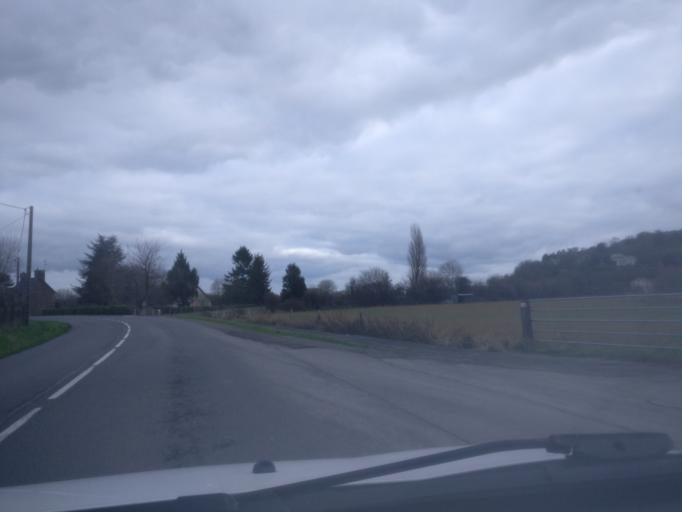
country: FR
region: Lower Normandy
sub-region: Departement de la Manche
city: Avranches
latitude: 48.6863
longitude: -1.3809
